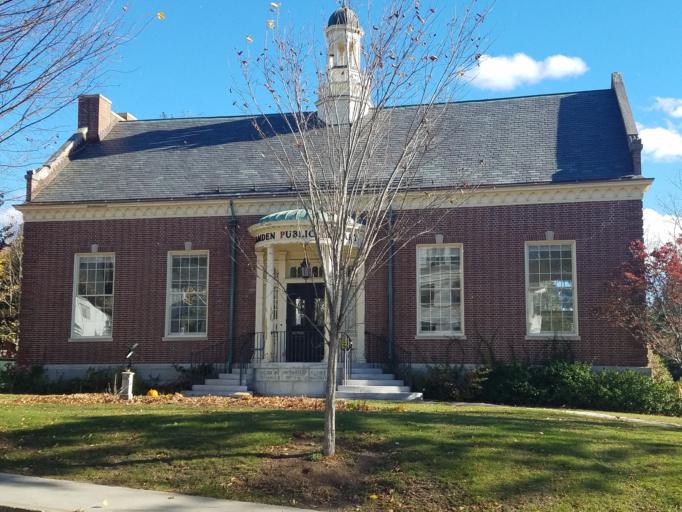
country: US
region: Maine
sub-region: Knox County
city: Camden
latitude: 44.2106
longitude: -69.0649
